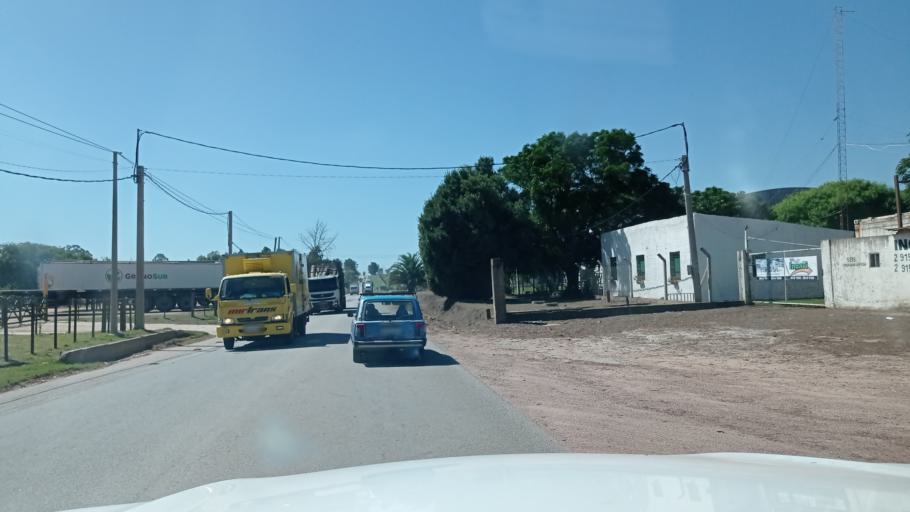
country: UY
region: Montevideo
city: Pajas Blancas
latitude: -34.8614
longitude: -56.2884
